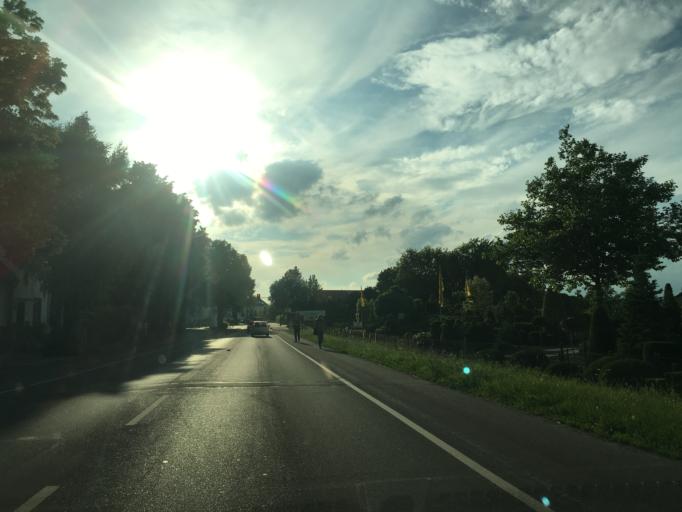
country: DE
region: North Rhine-Westphalia
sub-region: Regierungsbezirk Munster
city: Muenster
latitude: 51.9547
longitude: 7.5435
